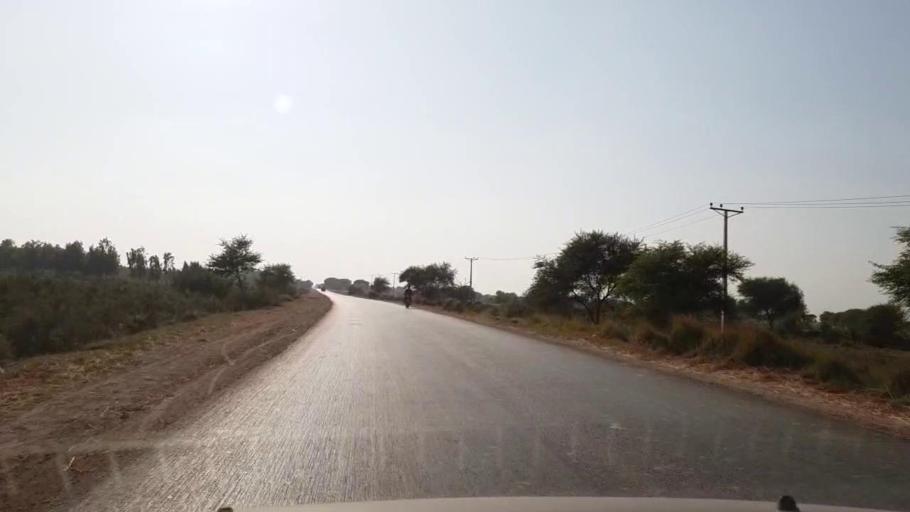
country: PK
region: Sindh
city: Tando Muhammad Khan
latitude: 25.0779
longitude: 68.4860
